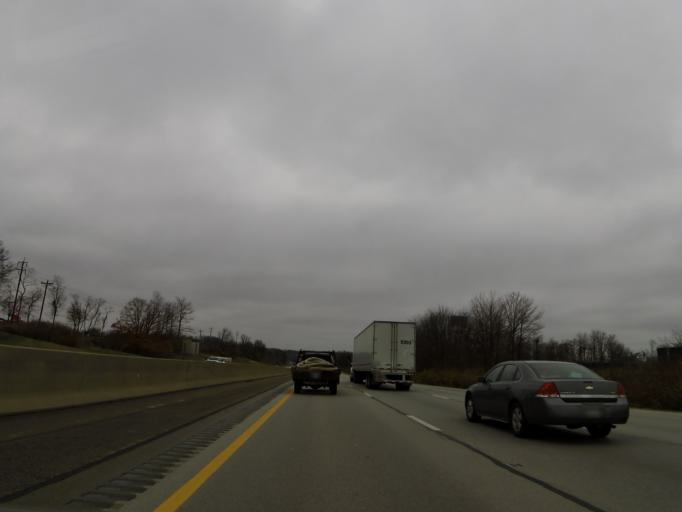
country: US
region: Kentucky
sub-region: Boone County
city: Walton
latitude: 38.8546
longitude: -84.6226
